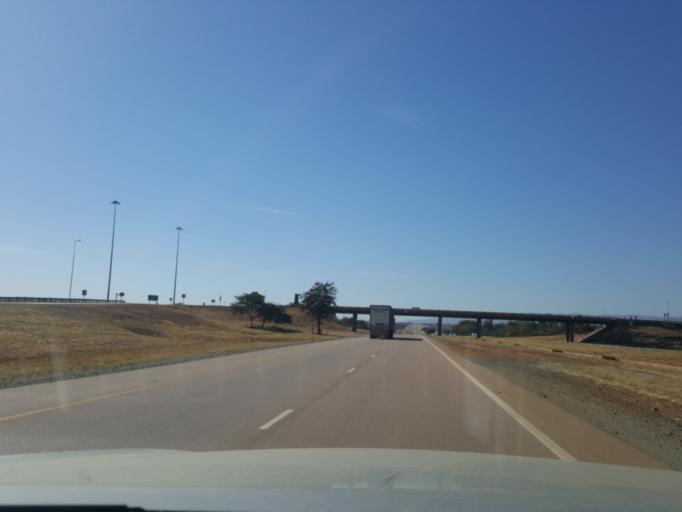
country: ZA
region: North-West
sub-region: Bojanala Platinum District Municipality
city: Brits
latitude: -25.7373
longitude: 27.5540
